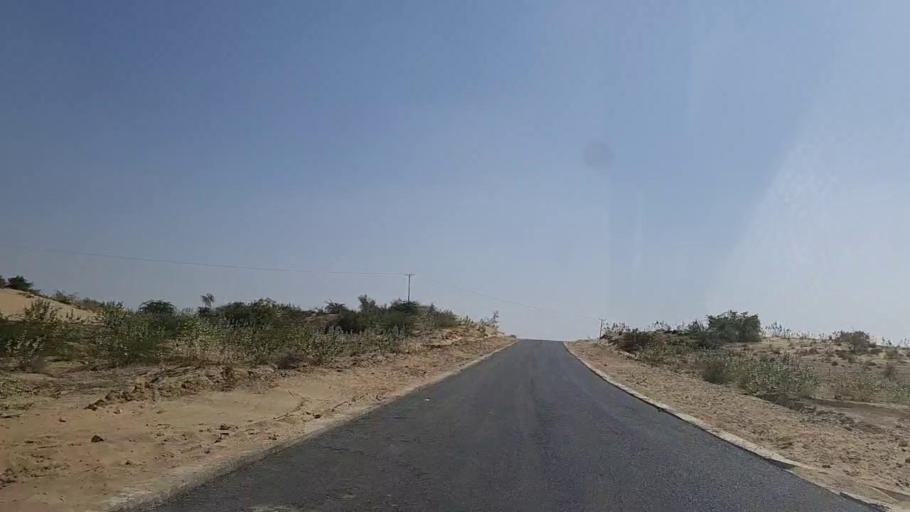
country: PK
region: Sindh
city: Diplo
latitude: 24.4800
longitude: 69.5280
